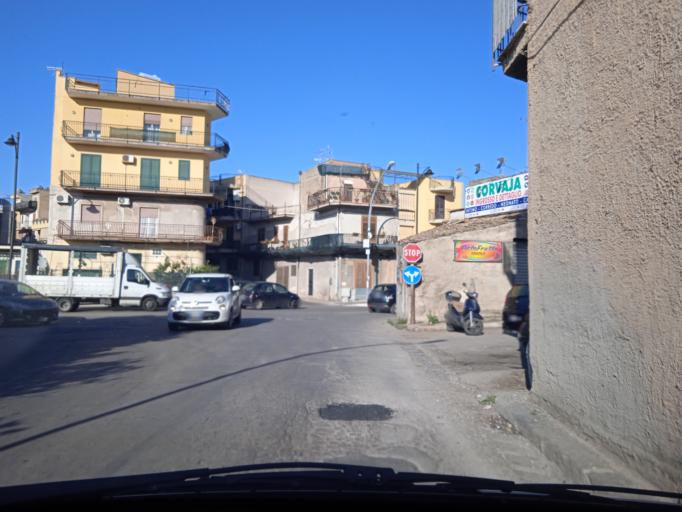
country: IT
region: Sicily
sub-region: Palermo
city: Ficarazzi
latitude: 38.0882
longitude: 13.4519
